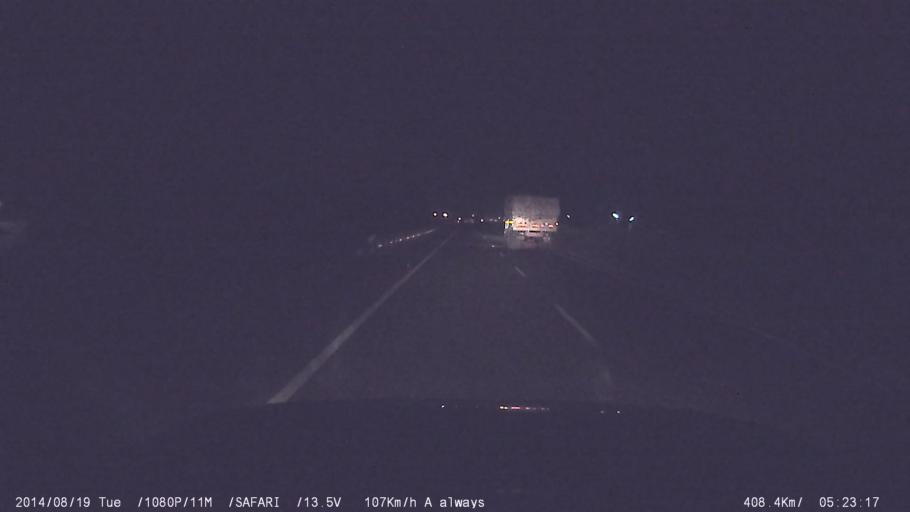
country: IN
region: Tamil Nadu
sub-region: Salem
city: Ilampillai
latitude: 11.5586
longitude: 78.0138
